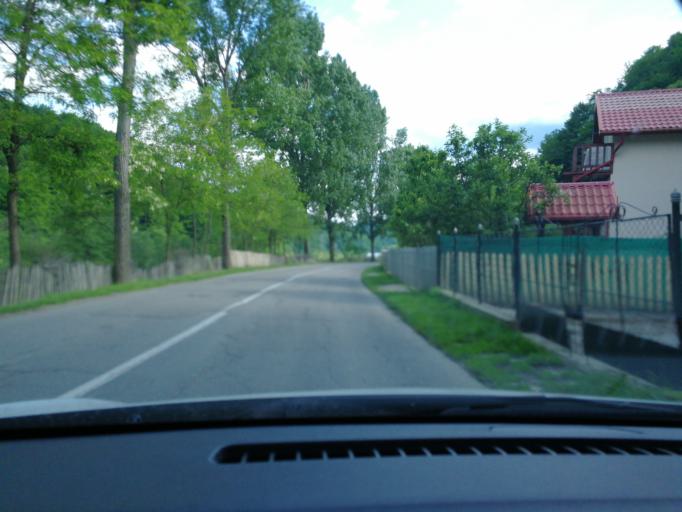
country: RO
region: Prahova
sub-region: Comuna Sotrile
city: Sotrile
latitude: 45.2344
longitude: 25.7312
